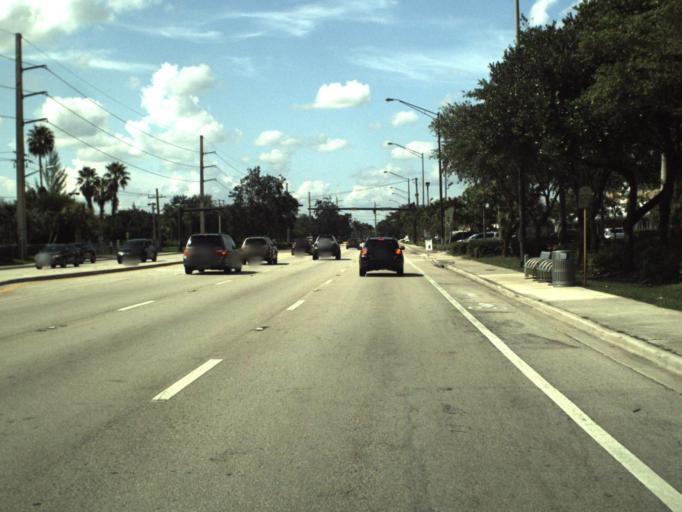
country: US
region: Florida
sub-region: Broward County
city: Plantation
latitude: 26.1576
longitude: -80.2571
